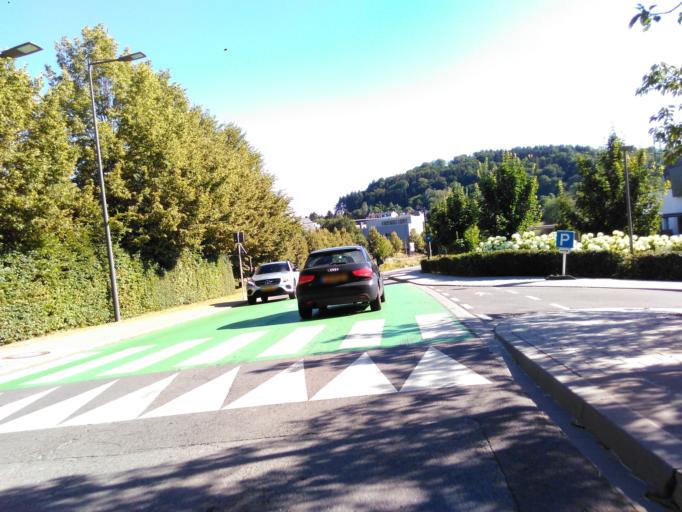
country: LU
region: Luxembourg
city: Belvaux
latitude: 49.5186
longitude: 5.9280
